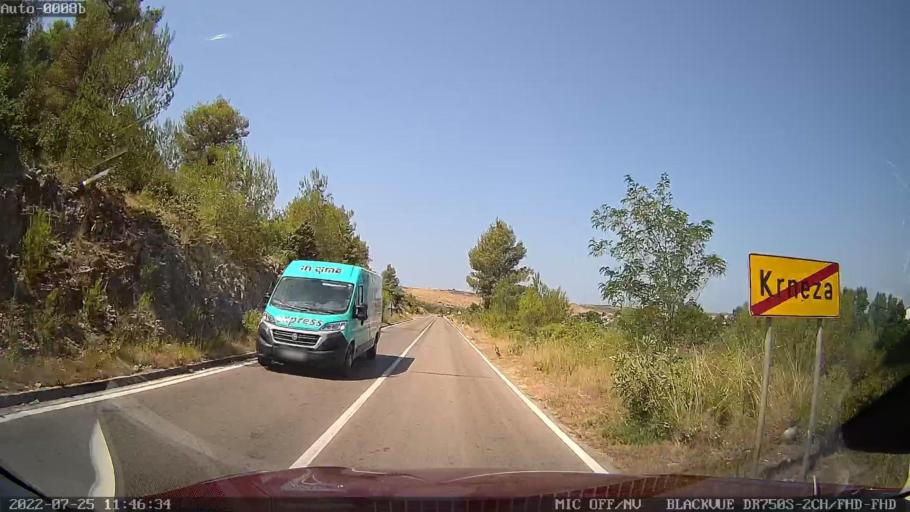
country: HR
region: Zadarska
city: Razanac
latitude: 44.2422
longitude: 15.3064
